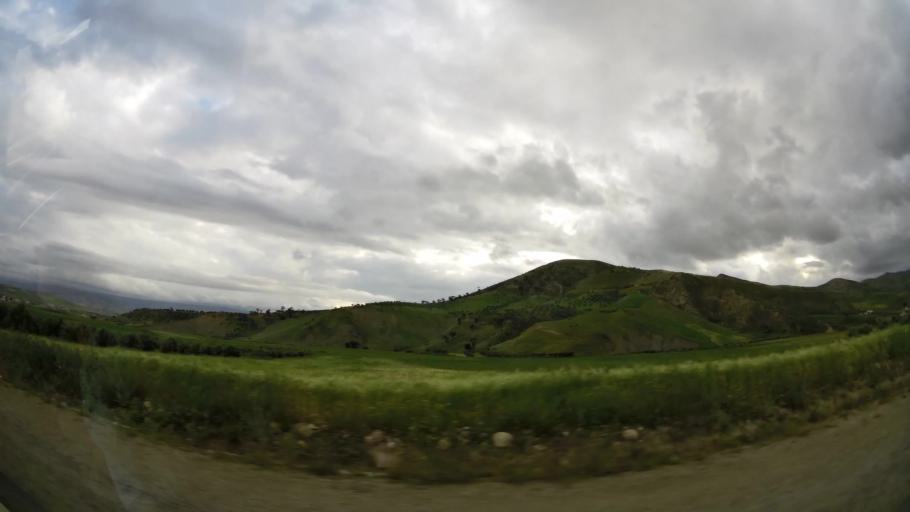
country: MA
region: Taza-Al Hoceima-Taounate
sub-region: Taza
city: Taza
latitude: 34.2840
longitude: -3.9599
